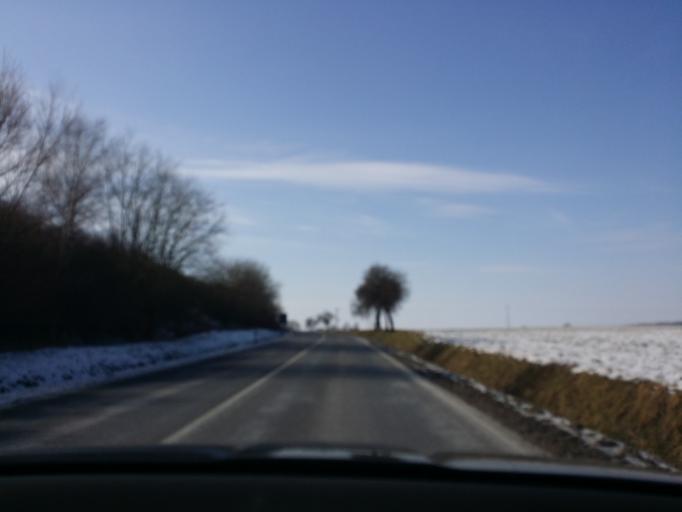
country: DE
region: Mecklenburg-Vorpommern
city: Wulkenzin
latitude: 53.5490
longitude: 13.2027
